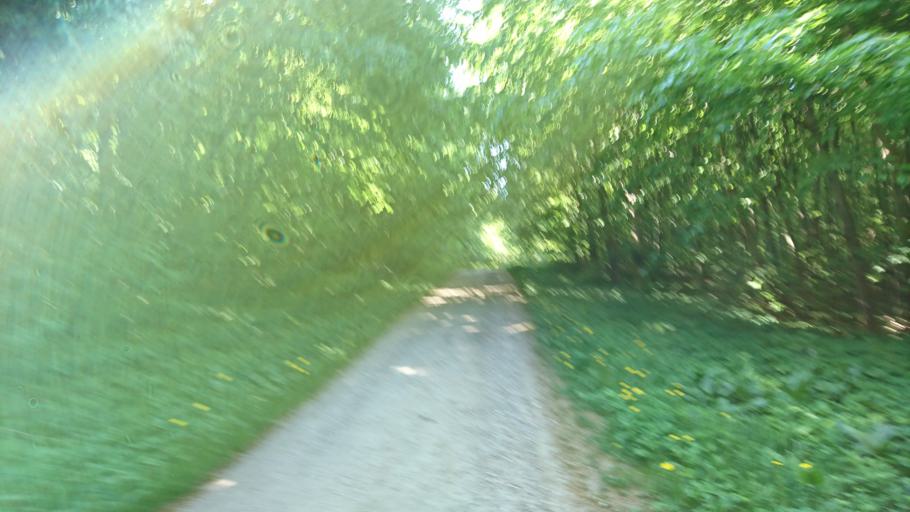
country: DK
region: Capital Region
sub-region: Ballerup Kommune
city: Malov
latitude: 55.7577
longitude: 12.3469
